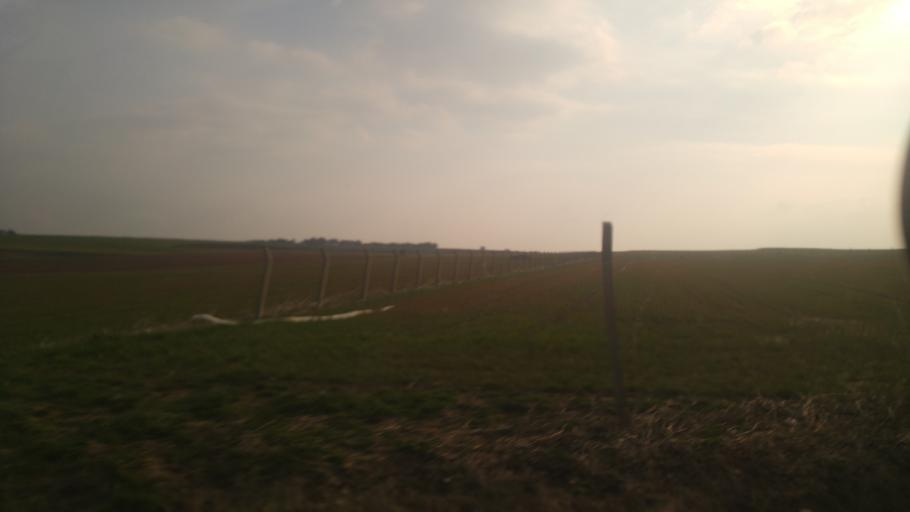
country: TR
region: Istanbul
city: Kavakli
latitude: 41.1289
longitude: 28.3435
